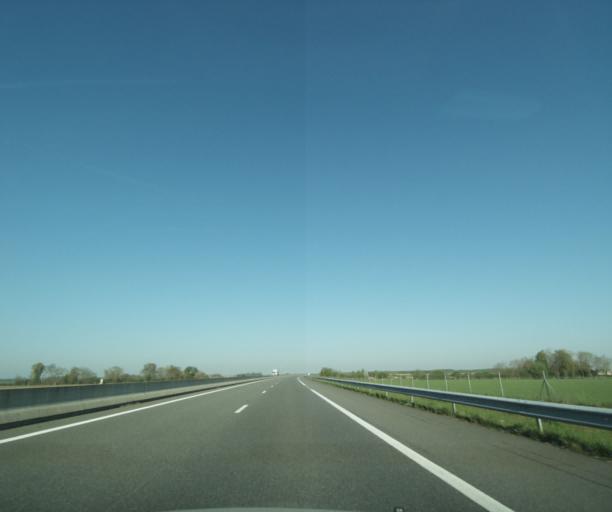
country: FR
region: Centre
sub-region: Departement du Loiret
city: Corbeilles
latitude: 48.0804
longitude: 2.6133
